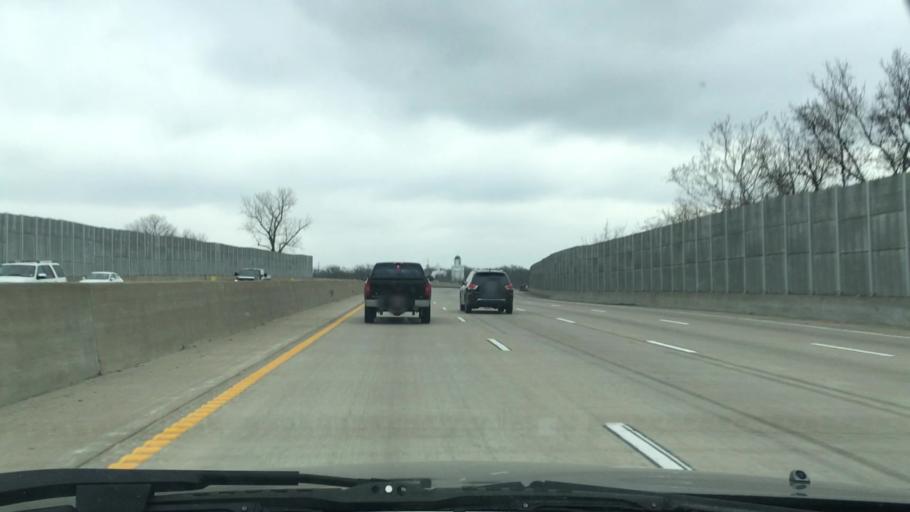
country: US
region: Missouri
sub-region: Saint Louis County
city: Frontenac
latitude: 38.6362
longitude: -90.3973
